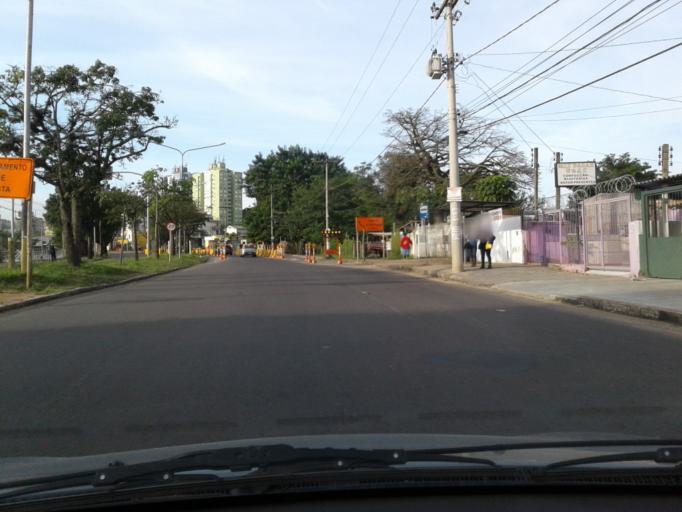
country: BR
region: Rio Grande do Sul
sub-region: Porto Alegre
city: Porto Alegre
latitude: -30.0944
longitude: -51.2439
